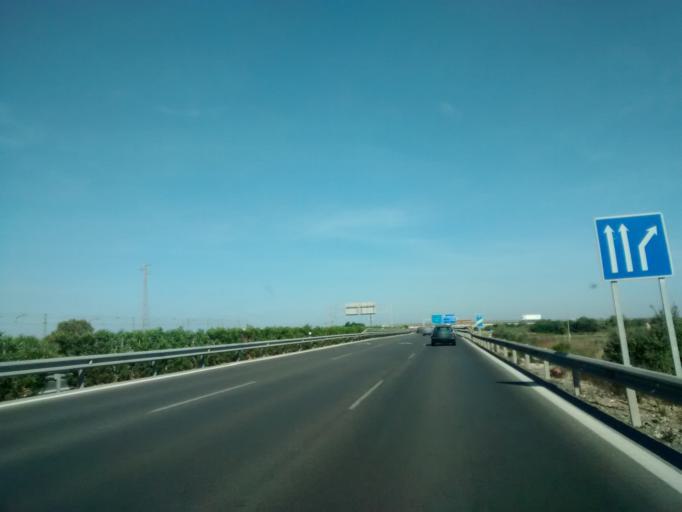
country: ES
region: Andalusia
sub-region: Provincia de Cadiz
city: San Fernando
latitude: 36.4645
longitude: -6.1629
